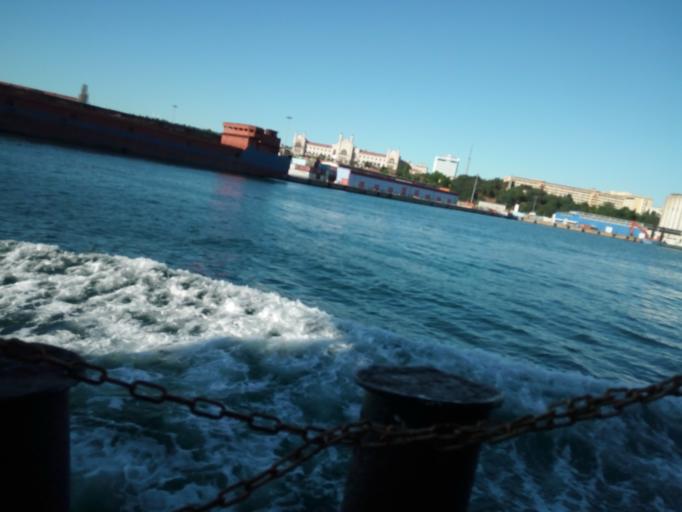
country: TR
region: Istanbul
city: UEskuedar
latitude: 40.9996
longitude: 29.0114
